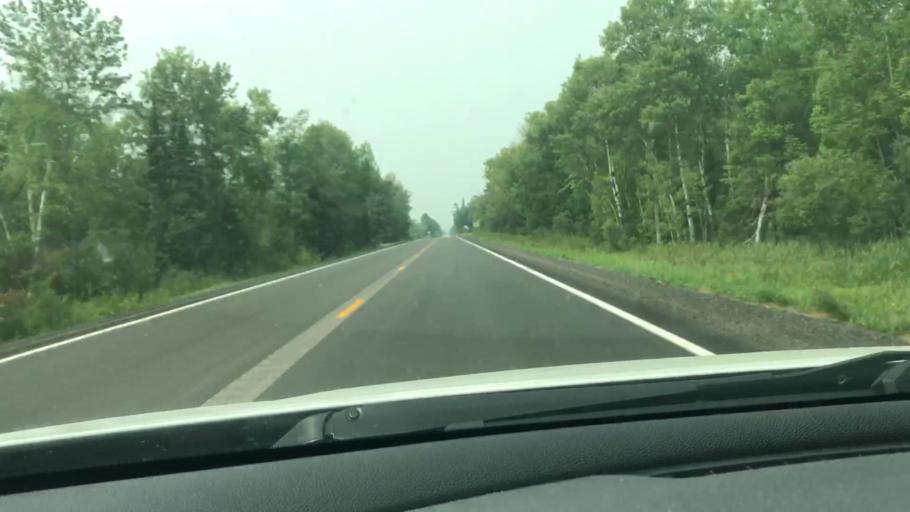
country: US
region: Minnesota
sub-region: Itasca County
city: Cohasset
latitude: 47.3653
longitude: -93.8748
